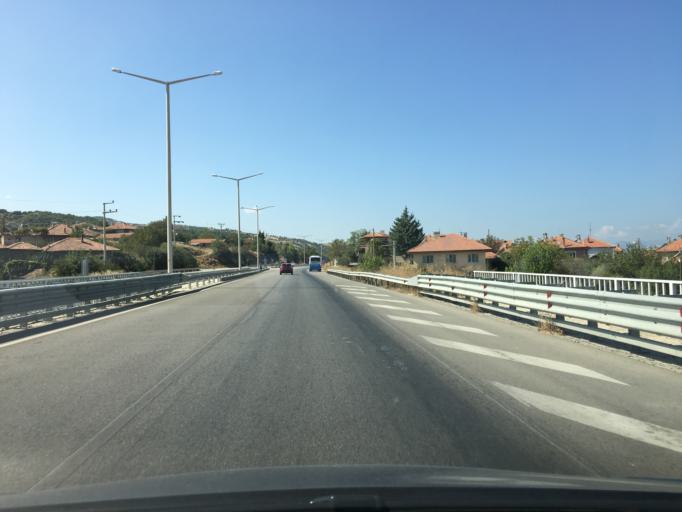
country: TR
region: Burdur
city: Burdur
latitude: 37.7597
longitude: 30.3438
